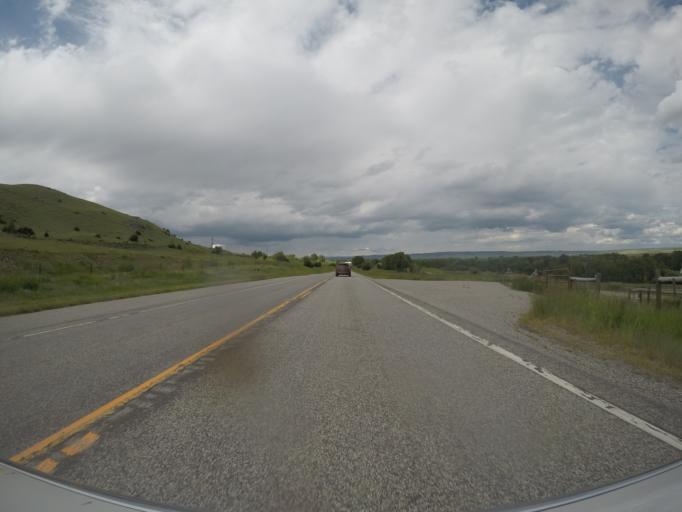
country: US
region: Montana
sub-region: Sweet Grass County
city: Big Timber
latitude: 45.8174
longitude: -109.9563
